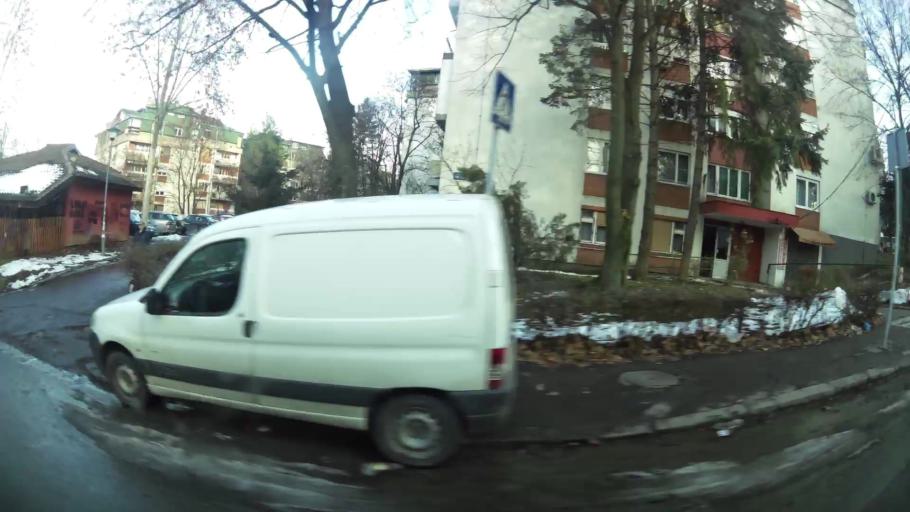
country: RS
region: Central Serbia
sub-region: Belgrade
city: Rakovica
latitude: 44.7468
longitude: 20.4546
